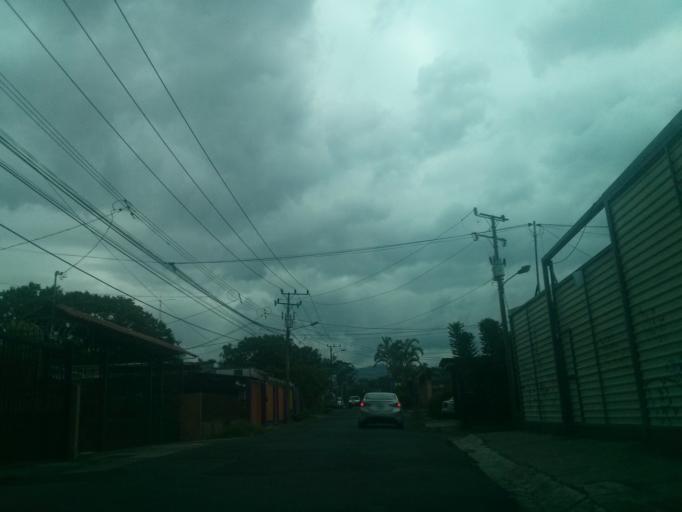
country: CR
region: San Jose
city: Curridabat
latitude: 9.9010
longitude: -84.0590
